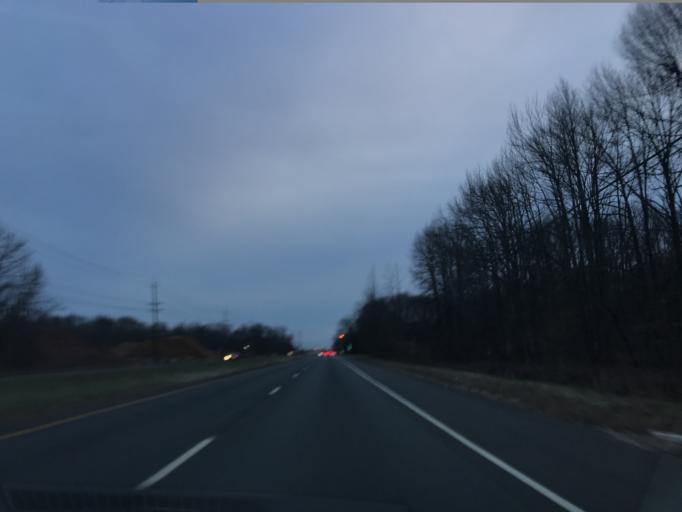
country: US
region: New Jersey
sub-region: Middlesex County
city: Dayton
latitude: 40.3869
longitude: -74.5042
